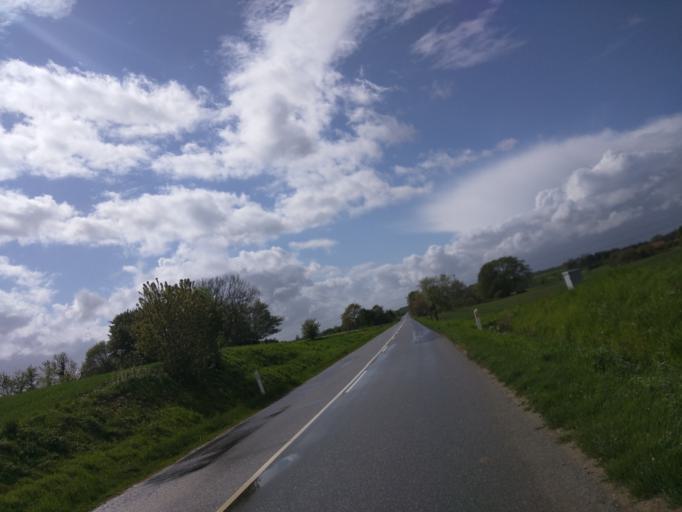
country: DK
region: Central Jutland
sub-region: Silkeborg Kommune
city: Kjellerup
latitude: 56.2769
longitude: 9.5054
